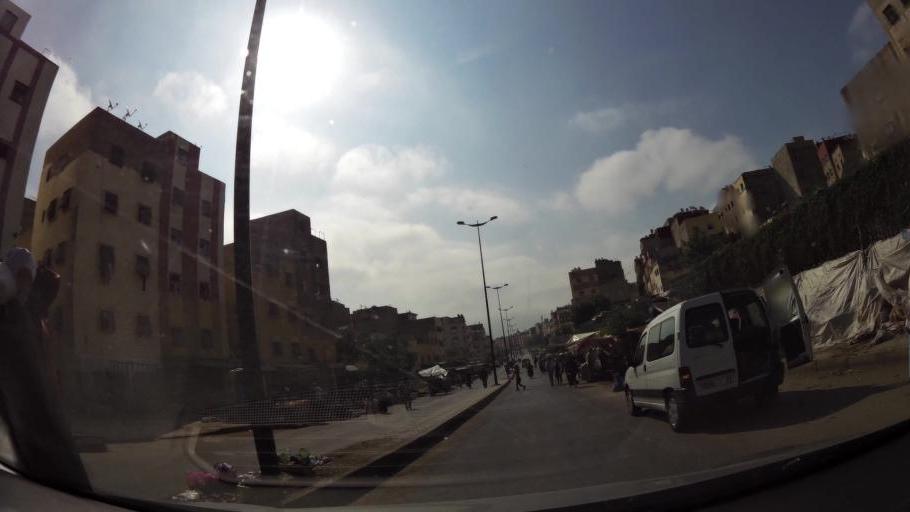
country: MA
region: Fes-Boulemane
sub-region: Fes
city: Fes
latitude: 34.0687
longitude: -5.0079
